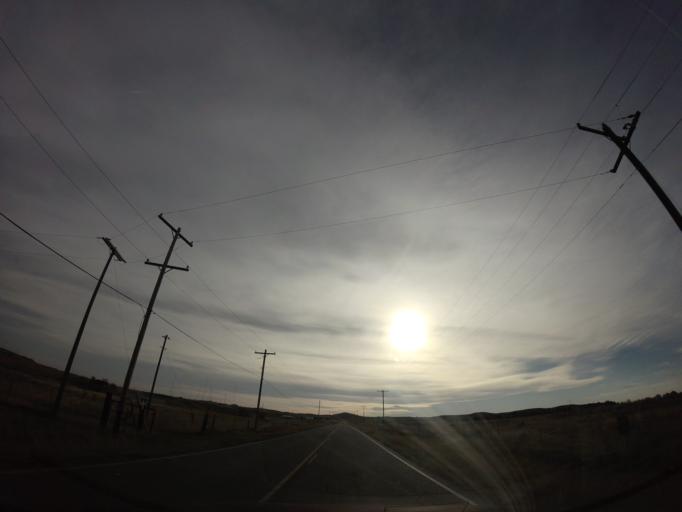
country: US
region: Montana
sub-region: Yellowstone County
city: Billings
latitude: 45.7841
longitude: -108.4596
